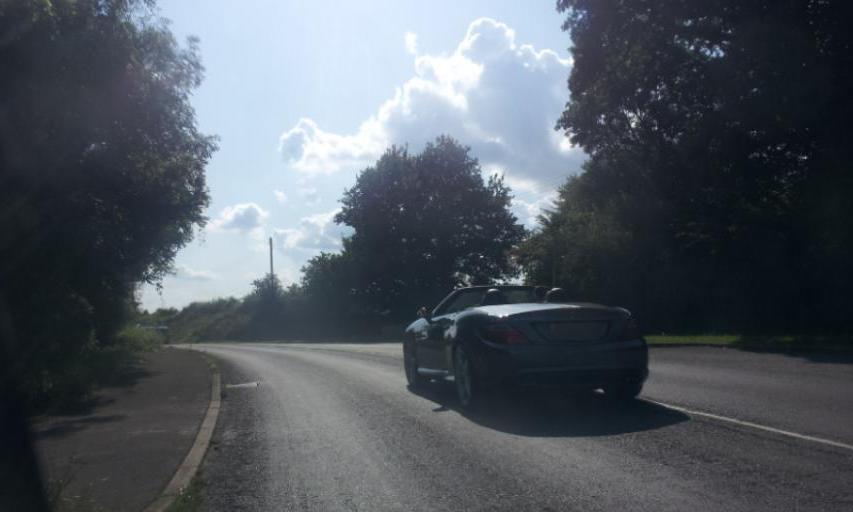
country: GB
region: England
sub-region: Kent
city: Wateringbury
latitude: 51.2451
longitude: 0.4116
